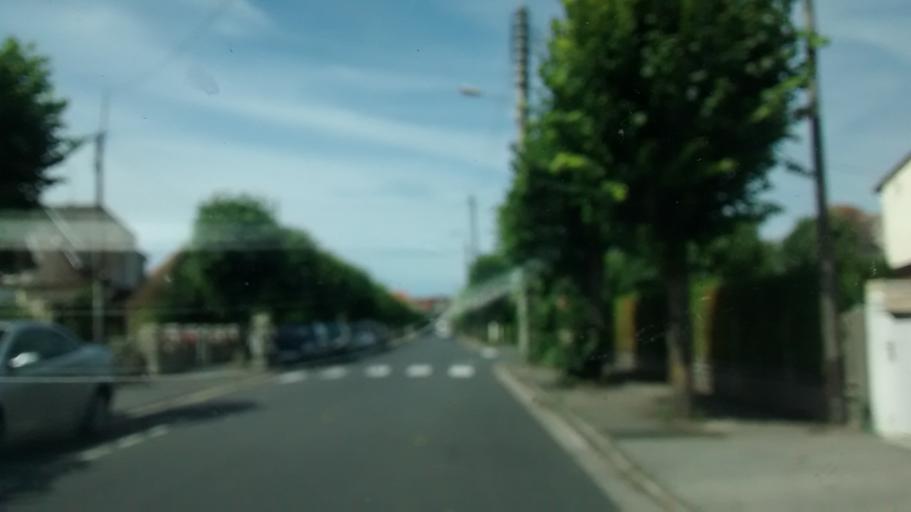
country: FR
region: Lower Normandy
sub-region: Departement du Calvados
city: Ouistreham
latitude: 49.2804
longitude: -0.2579
